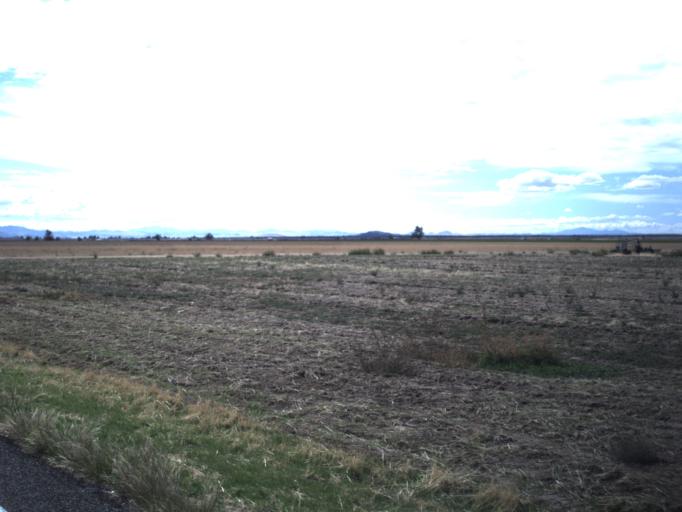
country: US
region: Utah
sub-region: Millard County
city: Fillmore
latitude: 39.0530
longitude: -112.4098
